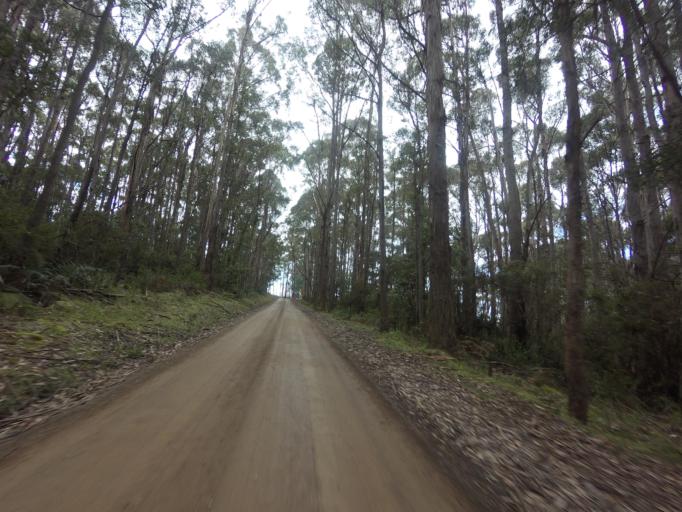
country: AU
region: Tasmania
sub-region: Huon Valley
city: Geeveston
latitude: -43.4226
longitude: 147.0105
